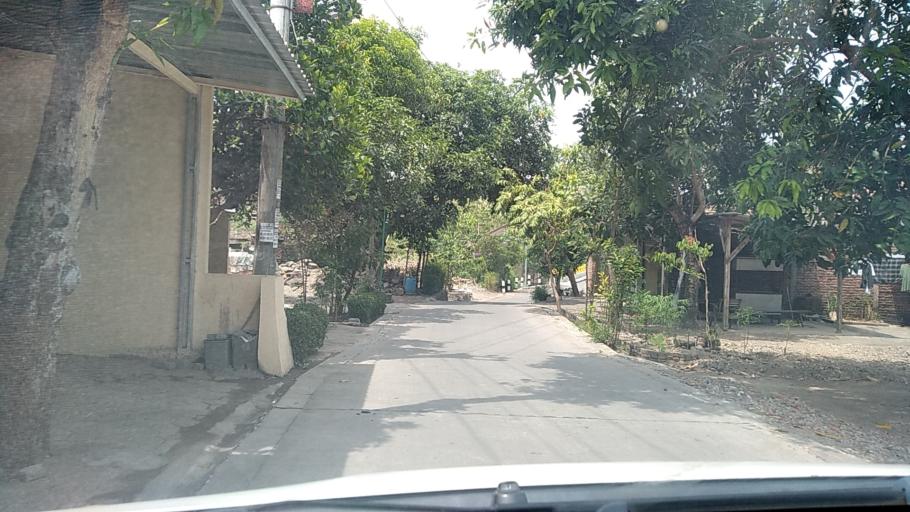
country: ID
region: Central Java
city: Mranggen
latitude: -7.0543
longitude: 110.4790
